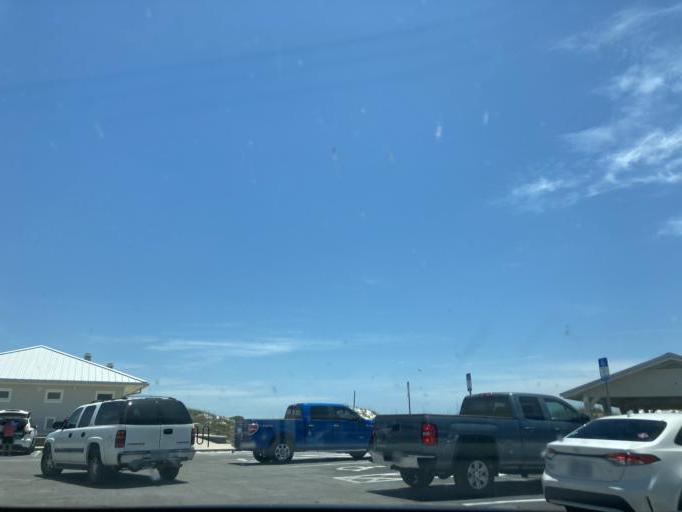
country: US
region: Florida
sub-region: Bay County
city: Lower Grand Lagoon
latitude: 30.1318
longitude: -85.7425
